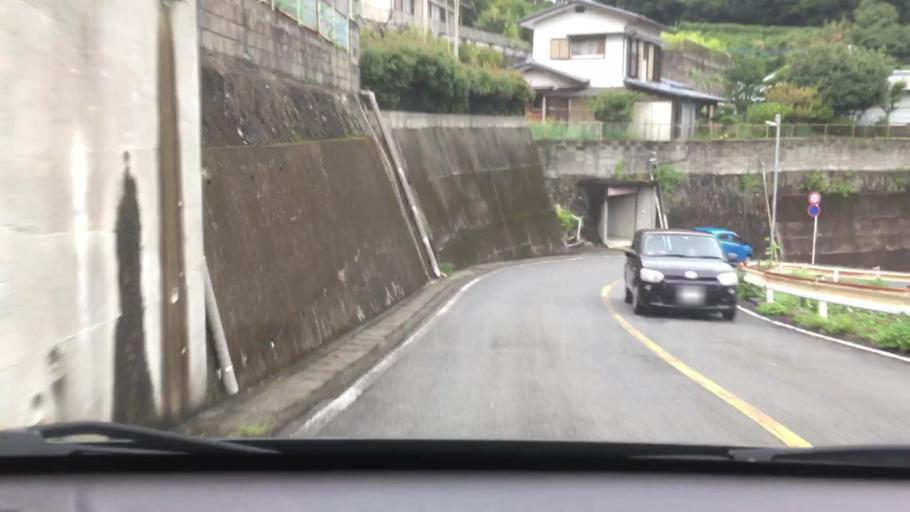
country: JP
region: Nagasaki
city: Nagasaki-shi
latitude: 32.7600
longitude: 129.9351
